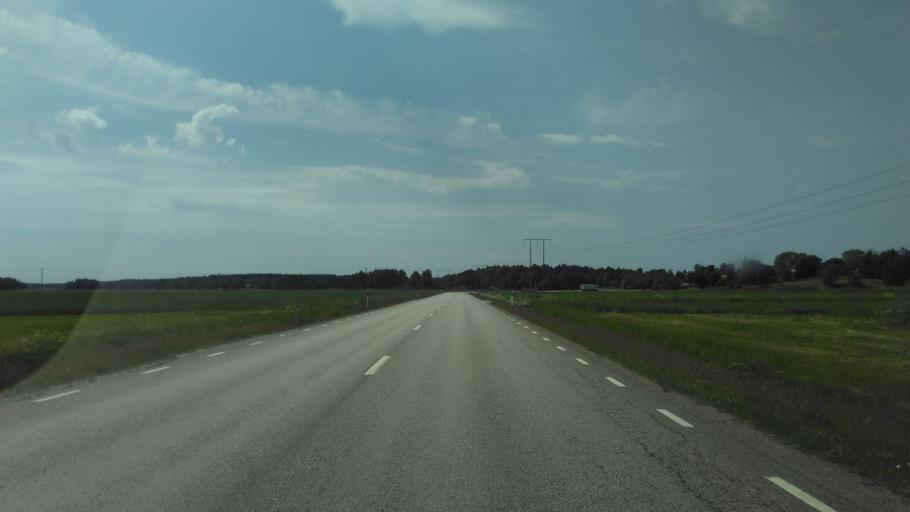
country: SE
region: Vaestra Goetaland
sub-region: Vara Kommun
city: Vara
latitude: 58.4399
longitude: 12.9477
